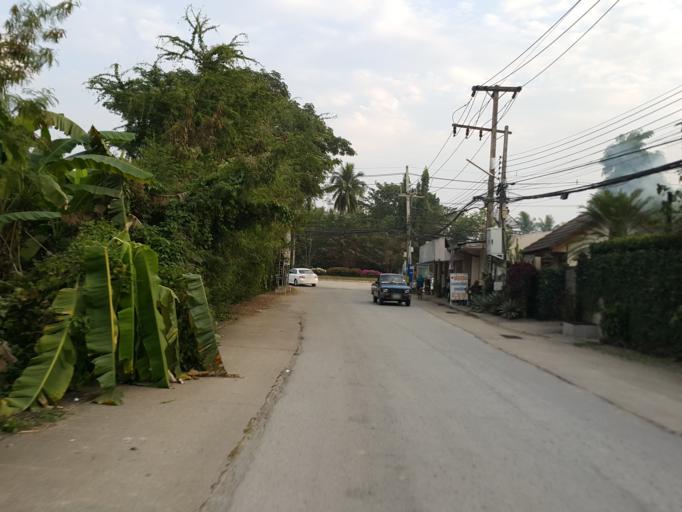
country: TH
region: Chiang Mai
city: San Sai
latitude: 18.8691
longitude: 99.1261
